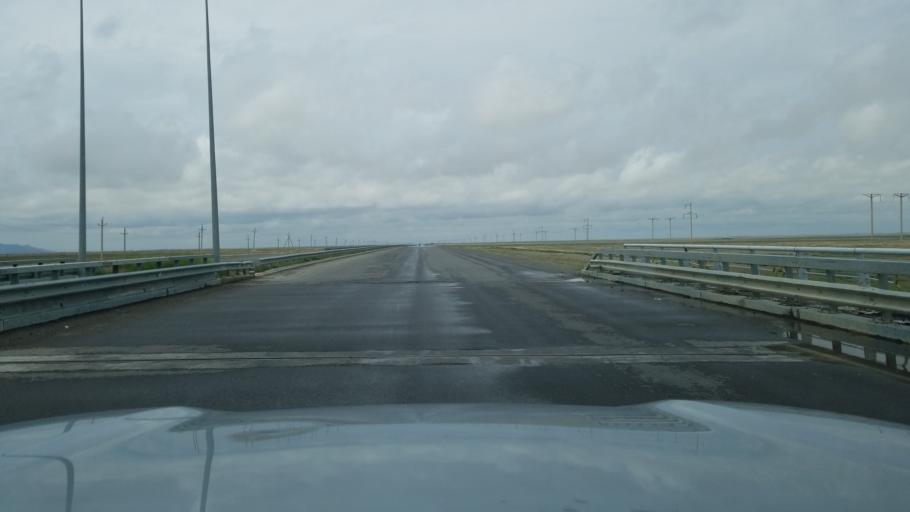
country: TM
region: Balkan
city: Gazanjyk
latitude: 39.1941
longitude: 55.7808
